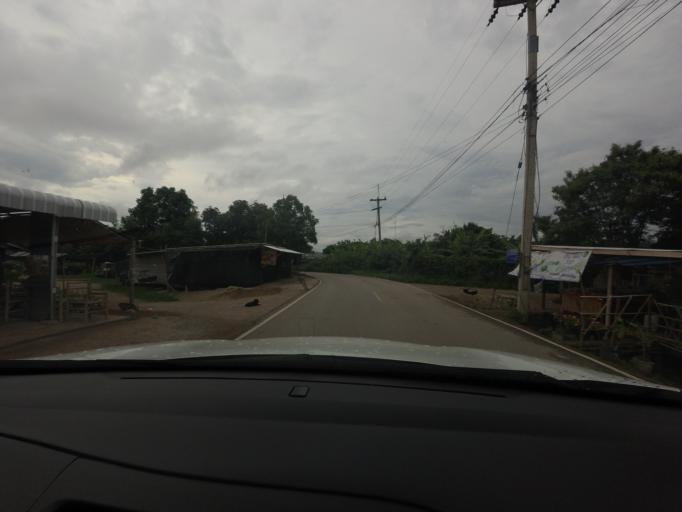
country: TH
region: Nakhon Ratchasima
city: Pak Chong
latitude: 14.6514
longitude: 101.4198
